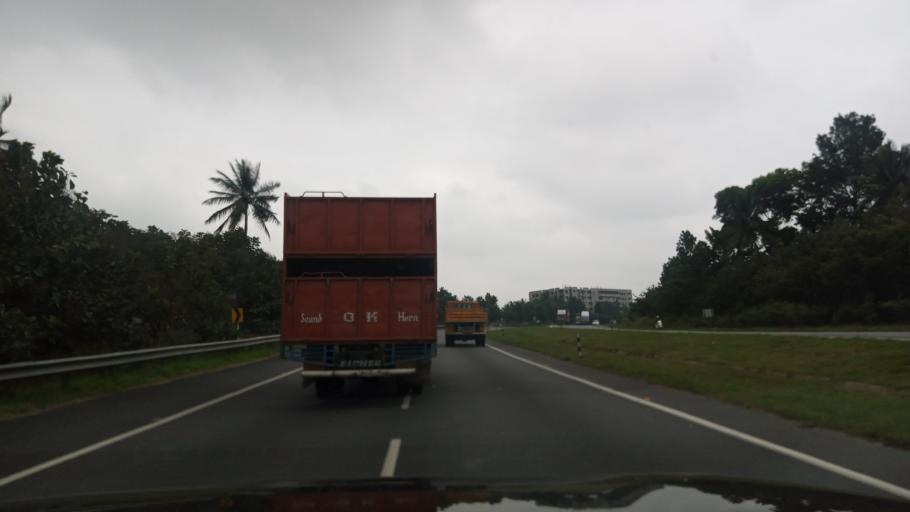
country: IN
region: Karnataka
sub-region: Bangalore Urban
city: Bangalore
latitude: 12.8519
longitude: 77.5927
